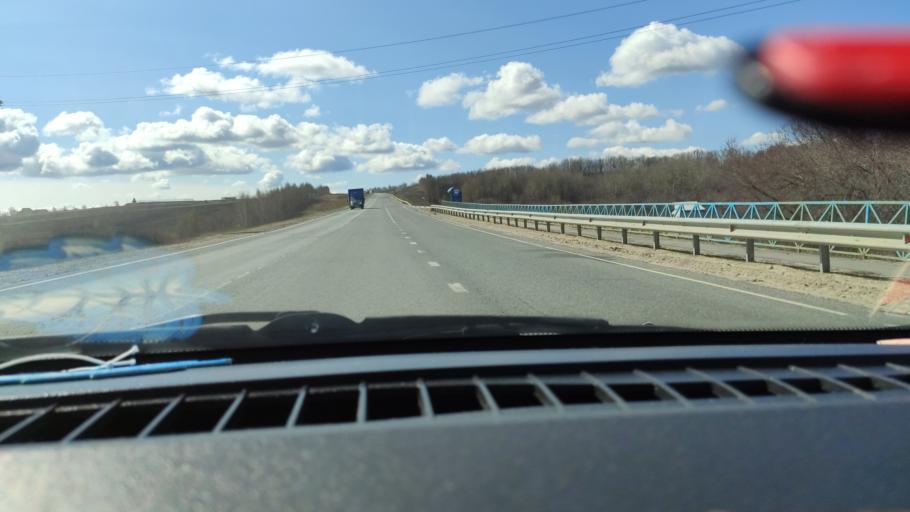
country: RU
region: Samara
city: Syzran'
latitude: 52.9630
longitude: 48.3069
